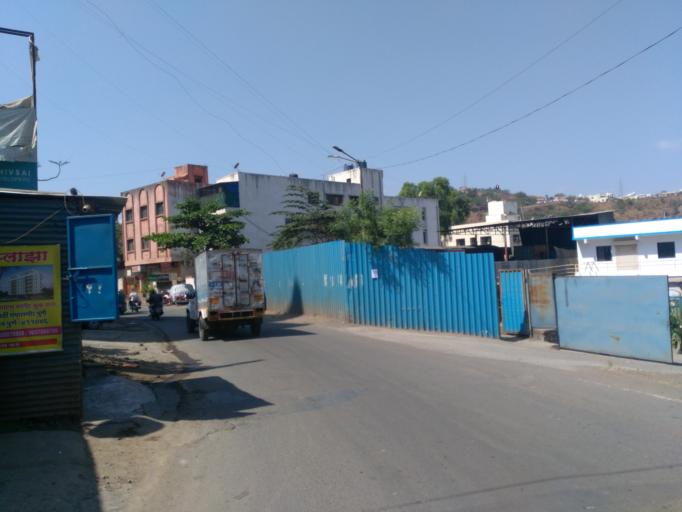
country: IN
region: Maharashtra
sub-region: Pune Division
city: Pune
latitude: 18.4393
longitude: 73.8631
